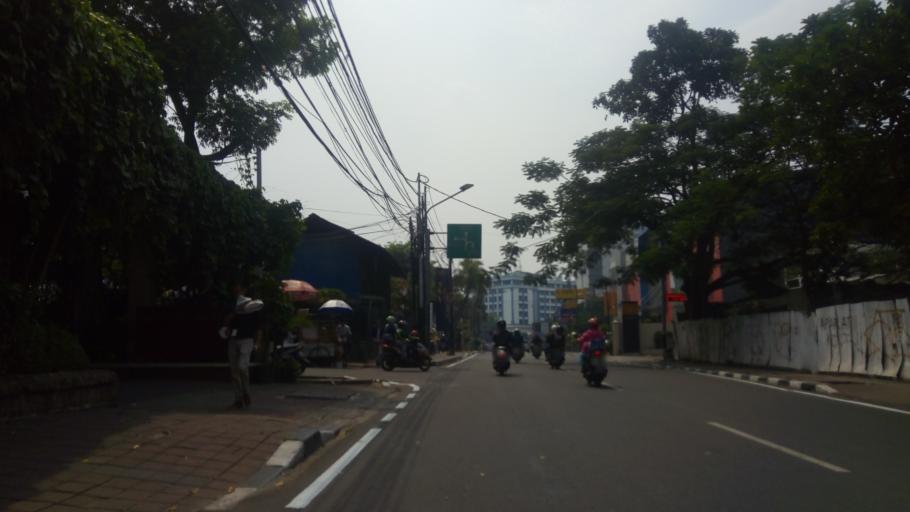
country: ID
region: Jakarta Raya
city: Jakarta
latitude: -6.1888
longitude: 106.8360
